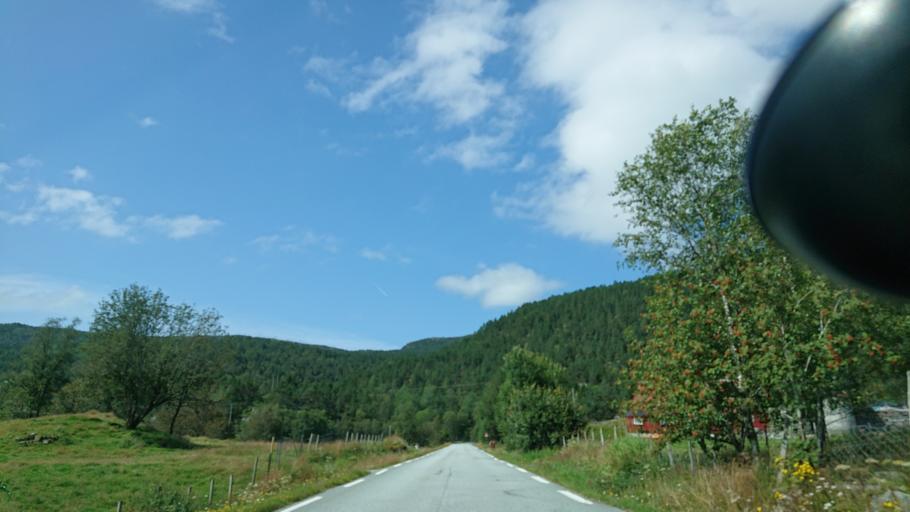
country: NO
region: Rogaland
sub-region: Hjelmeland
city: Hjelmelandsvagen
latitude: 59.2382
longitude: 6.2588
